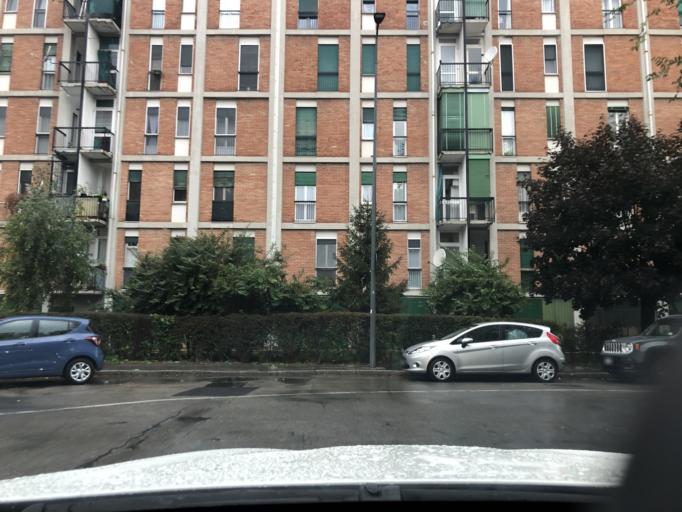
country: IT
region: Lombardy
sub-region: Citta metropolitana di Milano
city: Baranzate
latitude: 45.4927
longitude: 9.1223
